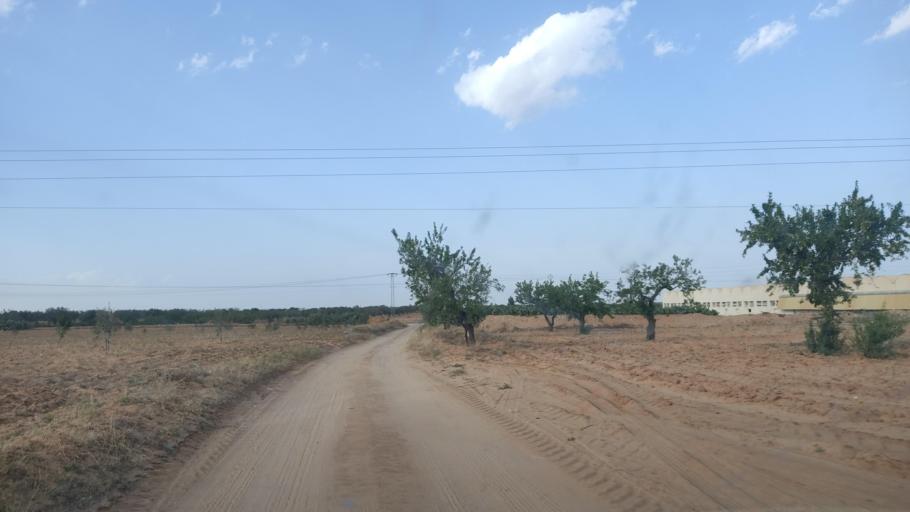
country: TN
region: Safaqis
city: Sfax
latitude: 34.8585
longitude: 10.6003
